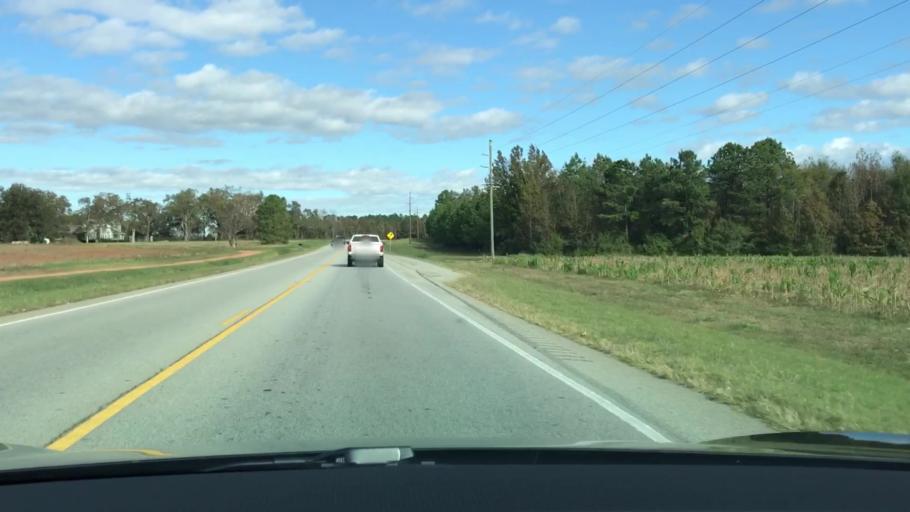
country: US
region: Georgia
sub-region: Jefferson County
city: Louisville
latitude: 33.0482
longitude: -82.4064
